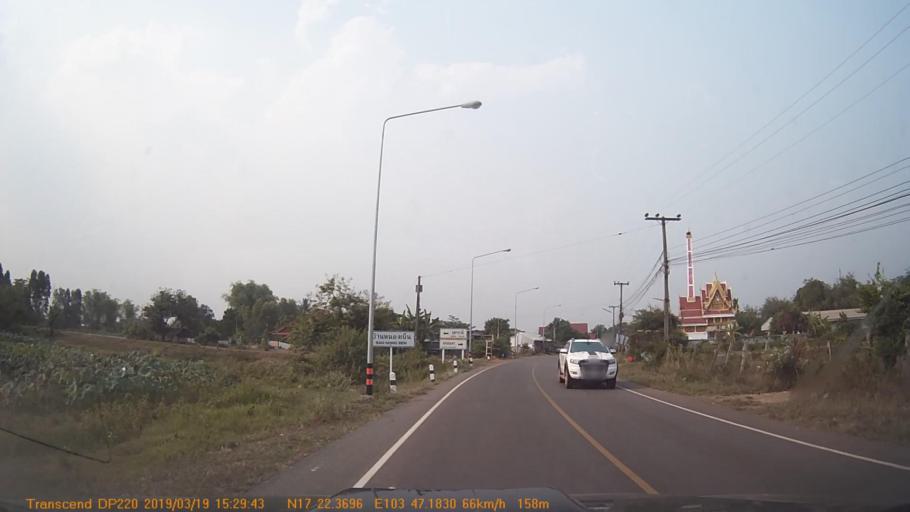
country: TH
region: Sakon Nakhon
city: Phanna Nikhom
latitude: 17.3732
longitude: 103.7863
